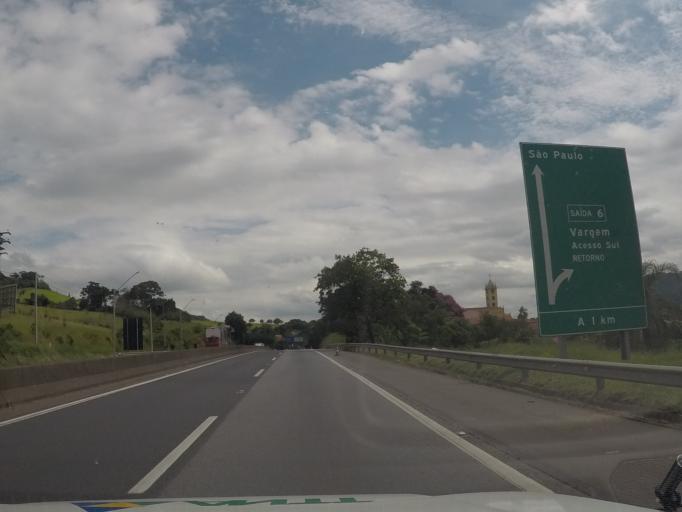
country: BR
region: Minas Gerais
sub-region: Extrema
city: Extrema
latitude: -22.8897
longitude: -46.4130
